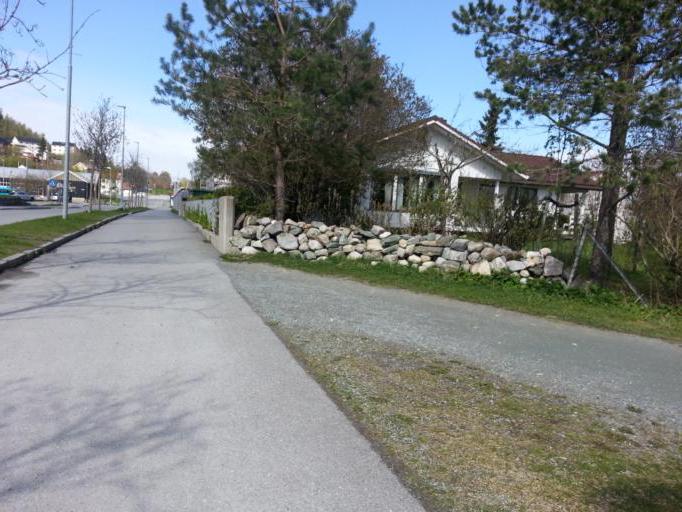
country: NO
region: Sor-Trondelag
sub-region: Trondheim
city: Trondheim
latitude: 63.3963
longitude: 10.3599
